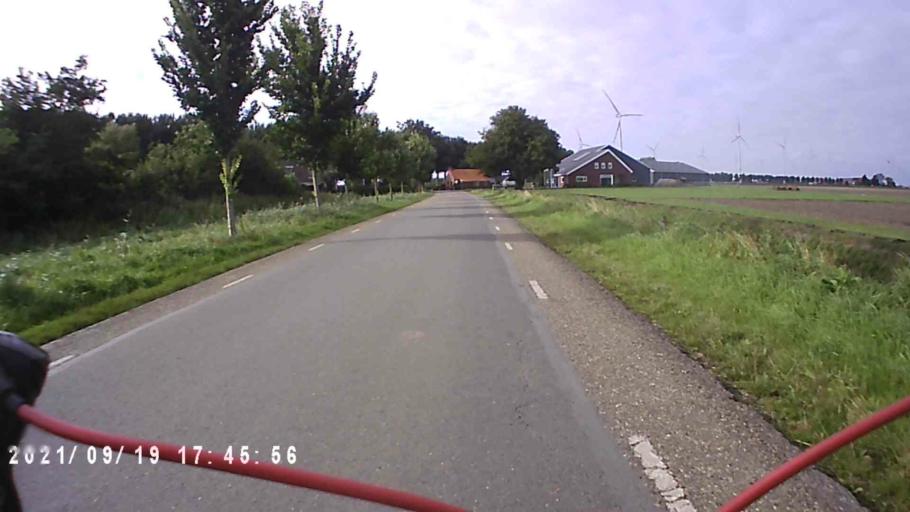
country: NL
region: Groningen
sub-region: Gemeente Delfzijl
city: Delfzijl
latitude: 53.2592
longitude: 6.9553
